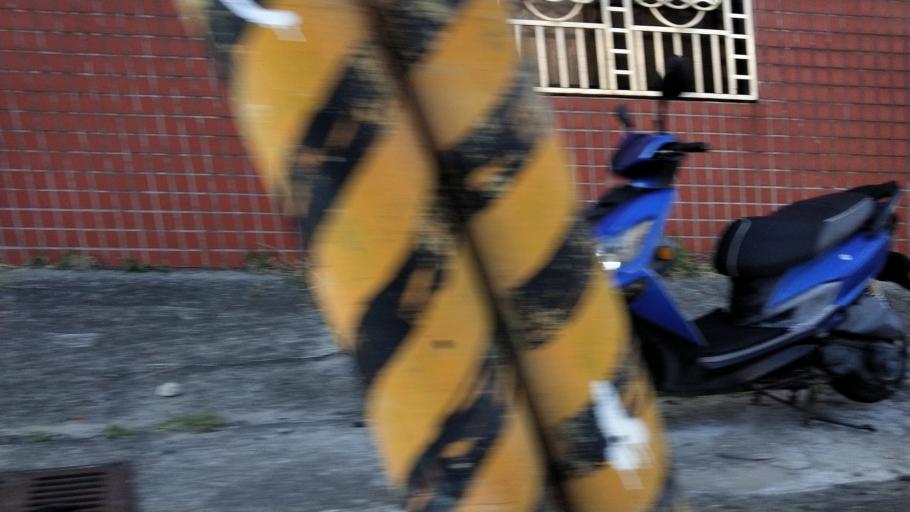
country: TW
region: Taiwan
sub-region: Miaoli
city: Miaoli
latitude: 24.5452
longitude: 120.6976
